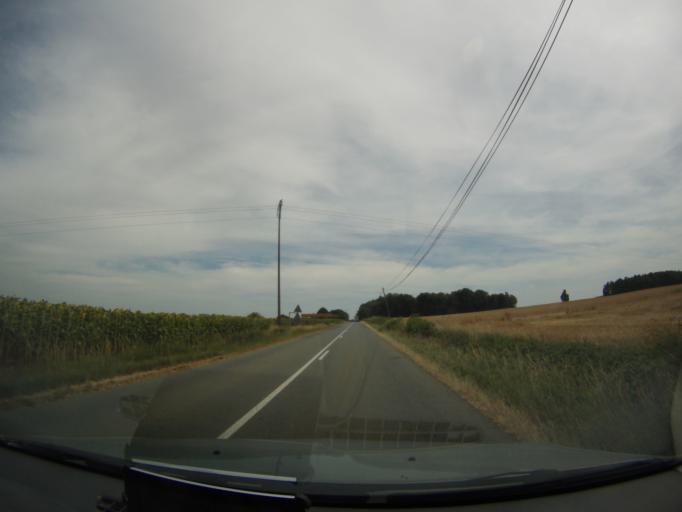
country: FR
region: Poitou-Charentes
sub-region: Departement de la Vienne
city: Mirebeau
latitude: 46.7521
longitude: 0.1708
